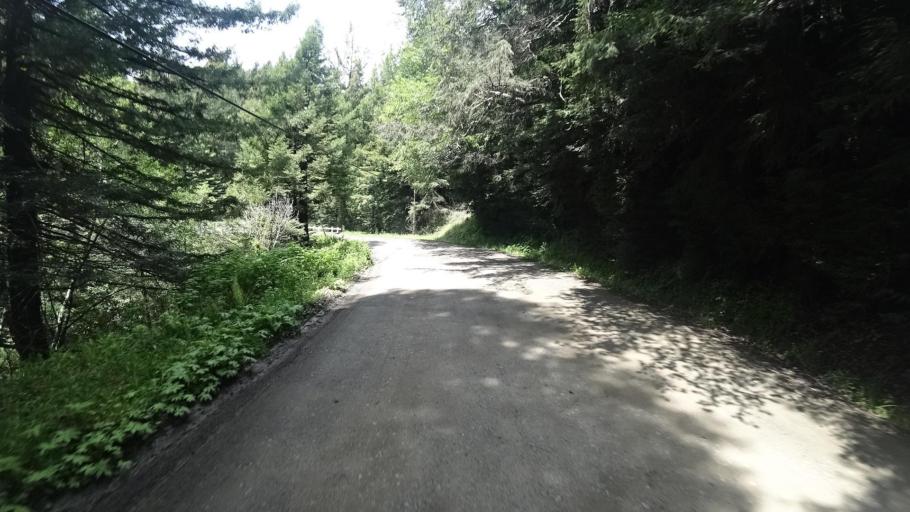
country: US
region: California
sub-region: Humboldt County
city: Blue Lake
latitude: 40.8457
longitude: -123.8938
